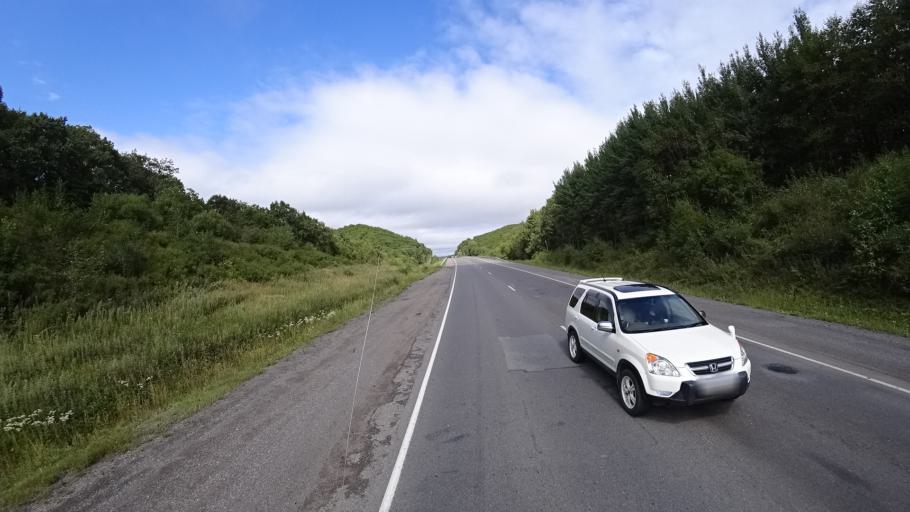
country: RU
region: Primorskiy
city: Lyalichi
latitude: 44.1237
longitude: 132.4224
